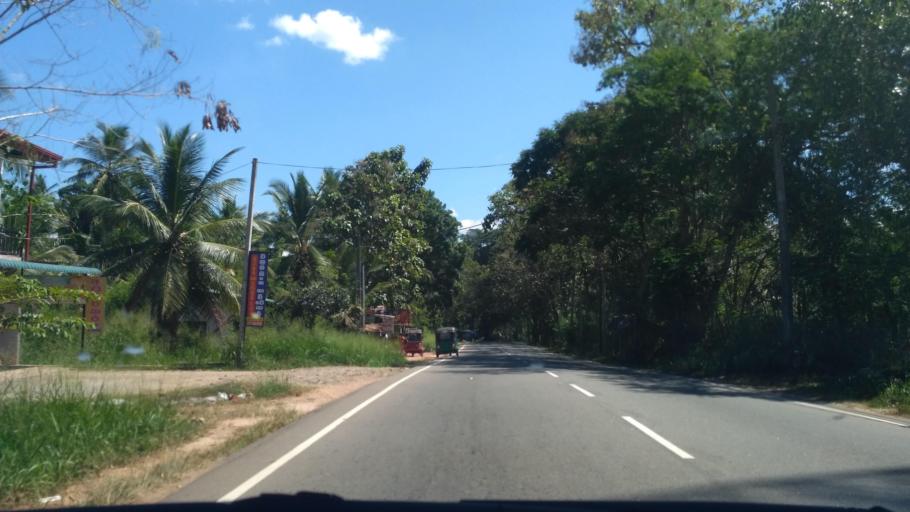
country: LK
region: North Western
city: Kuliyapitiya
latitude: 7.3240
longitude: 80.0723
